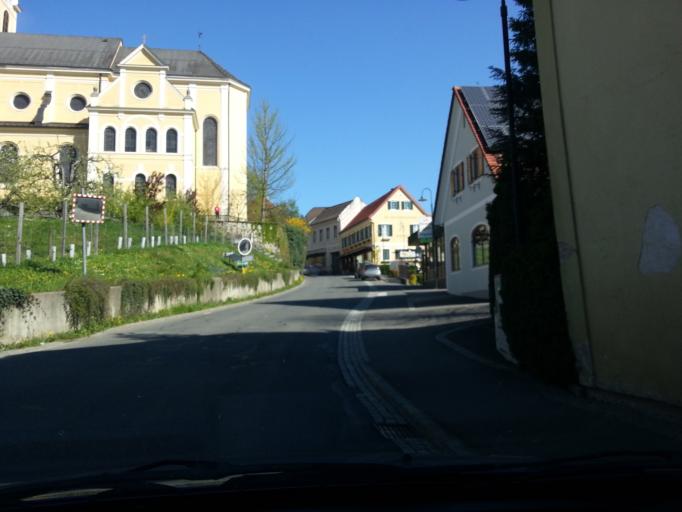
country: AT
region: Styria
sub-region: Politischer Bezirk Leibnitz
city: Leutschach
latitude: 46.6666
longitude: 15.4689
